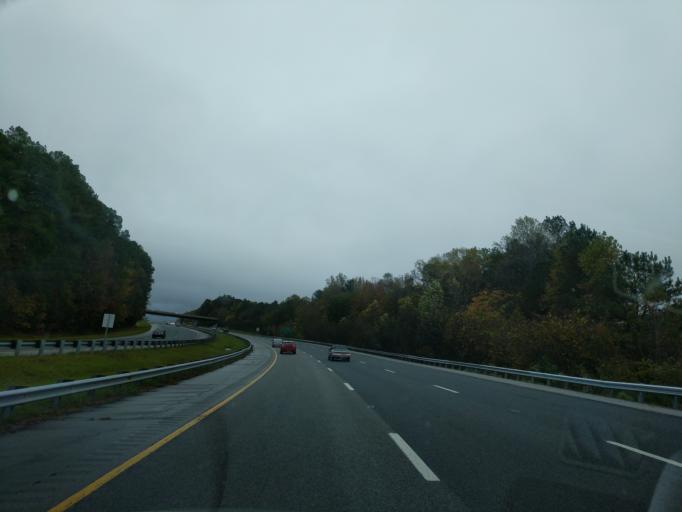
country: US
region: North Carolina
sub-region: Orange County
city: Hillsborough
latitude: 36.0595
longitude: -79.1307
